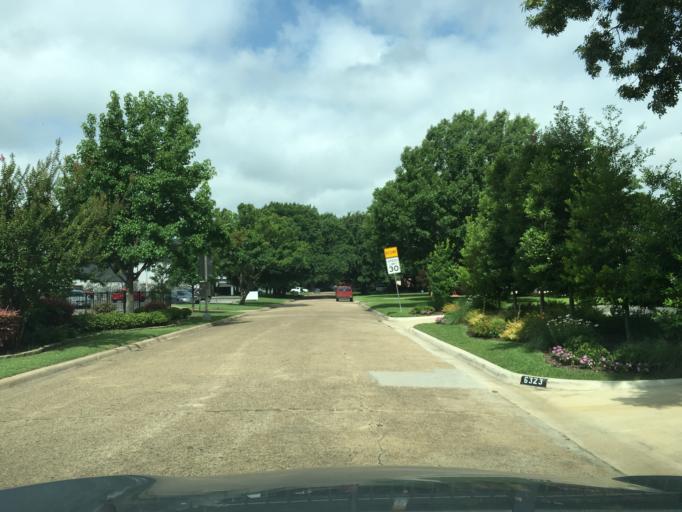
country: US
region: Texas
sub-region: Dallas County
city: University Park
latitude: 32.8812
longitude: -96.7968
